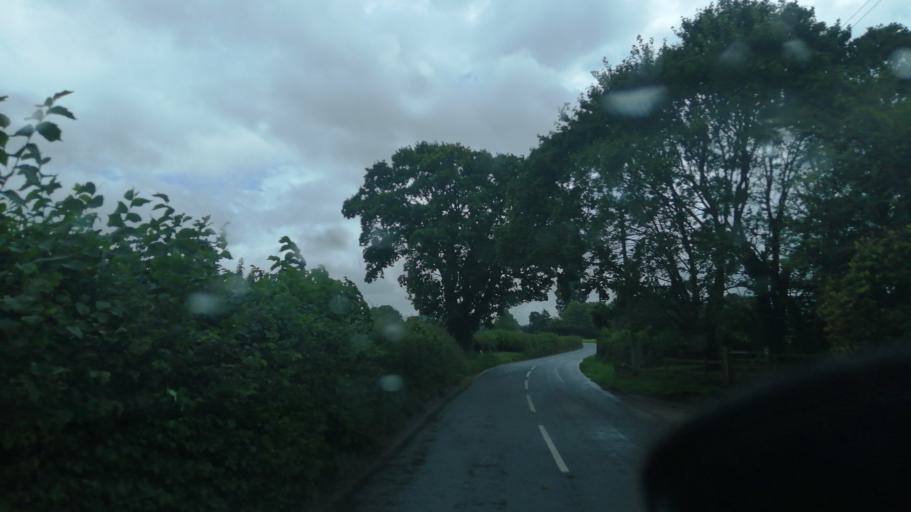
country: GB
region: England
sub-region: Herefordshire
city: Kingstone
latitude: 52.0188
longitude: -2.8505
